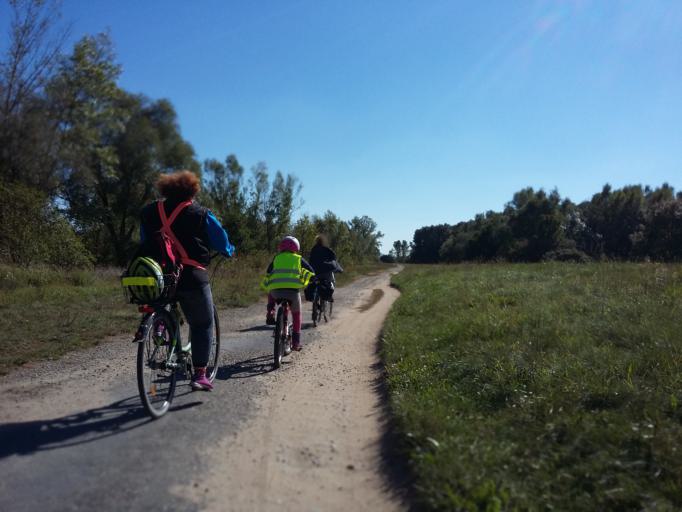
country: AT
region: Lower Austria
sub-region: Politischer Bezirk Ganserndorf
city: Marchegg
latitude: 48.3191
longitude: 16.9107
